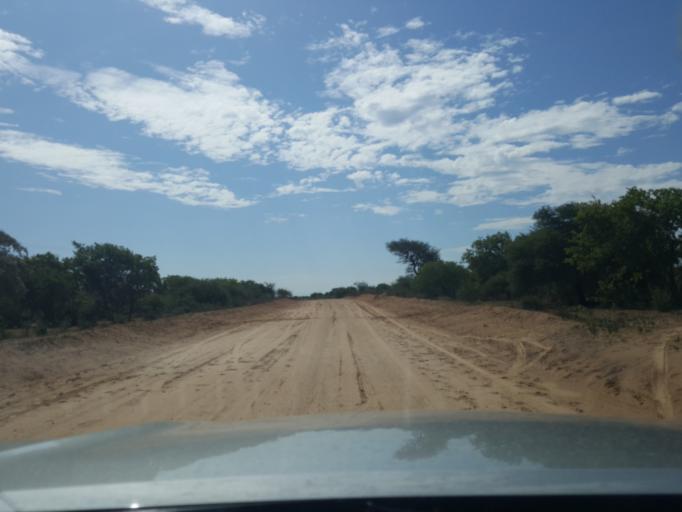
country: BW
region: Kweneng
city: Khudumelapye
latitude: -23.8627
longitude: 24.8872
